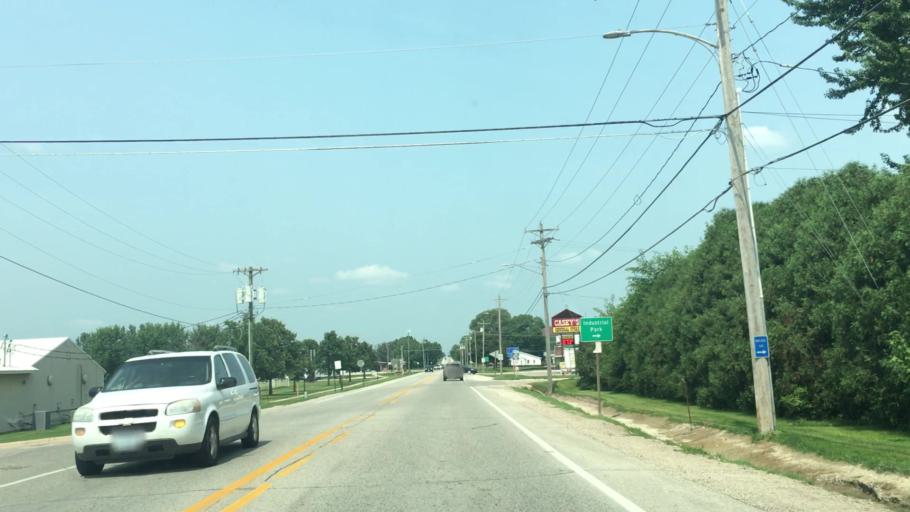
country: US
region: Iowa
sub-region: Buchanan County
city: Independence
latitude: 42.4791
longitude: -91.8894
